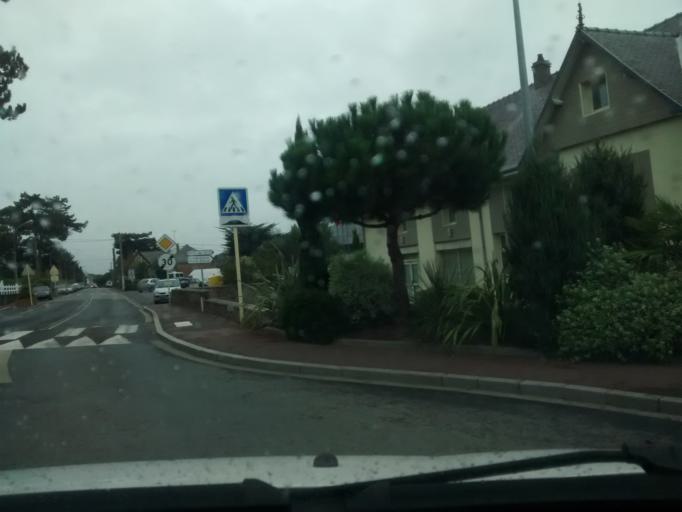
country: FR
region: Lower Normandy
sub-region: Departement de la Manche
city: Jullouville
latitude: 48.7705
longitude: -1.5675
